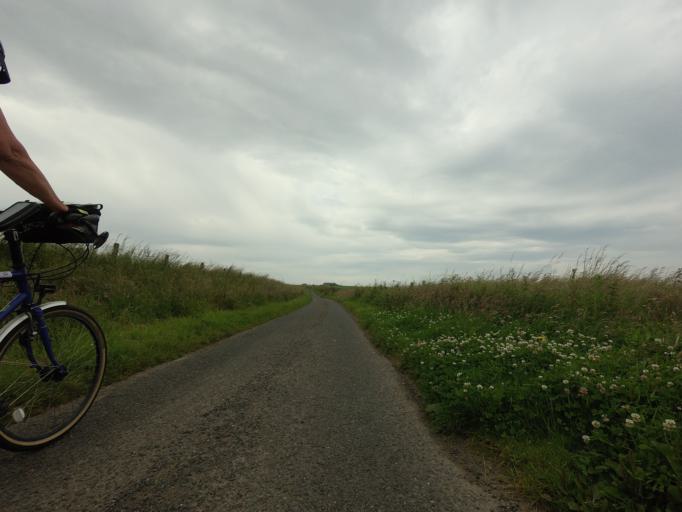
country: GB
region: Scotland
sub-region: Aberdeenshire
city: Whitehills
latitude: 57.6776
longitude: -2.5915
